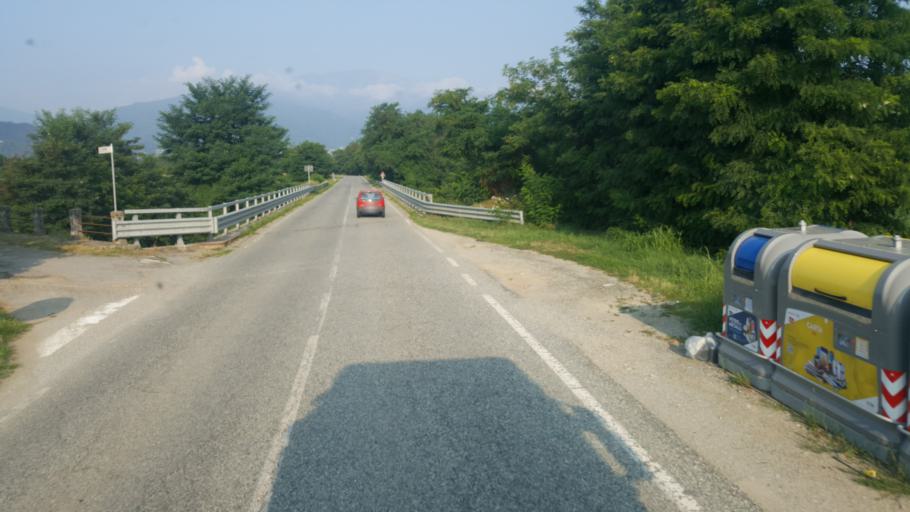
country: IT
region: Piedmont
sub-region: Provincia di Torino
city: Cavour
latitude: 44.7435
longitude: 7.3810
